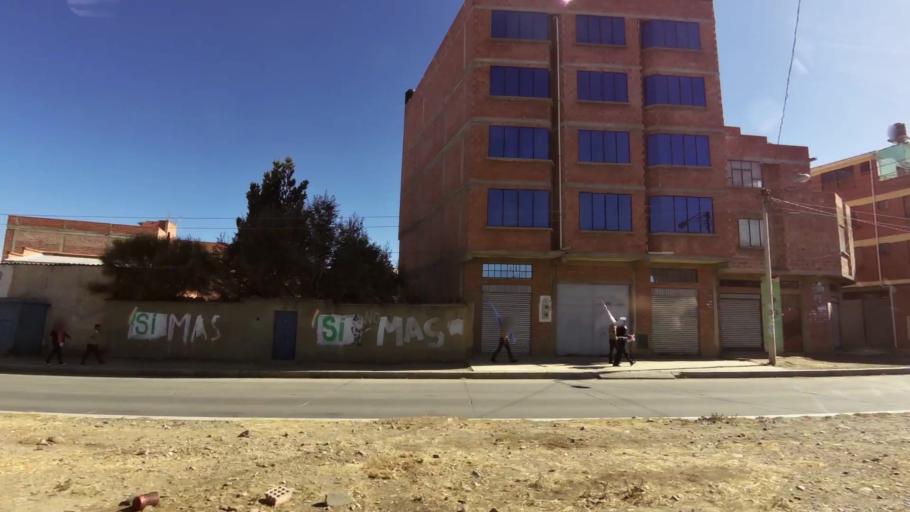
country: BO
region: La Paz
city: La Paz
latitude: -16.5277
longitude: -68.2053
